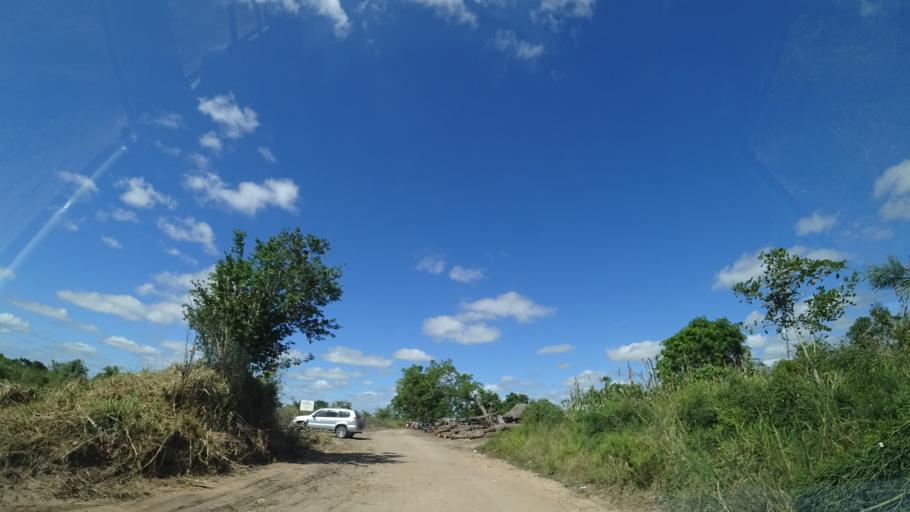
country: MZ
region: Sofala
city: Dondo
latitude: -19.2715
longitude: 34.6790
